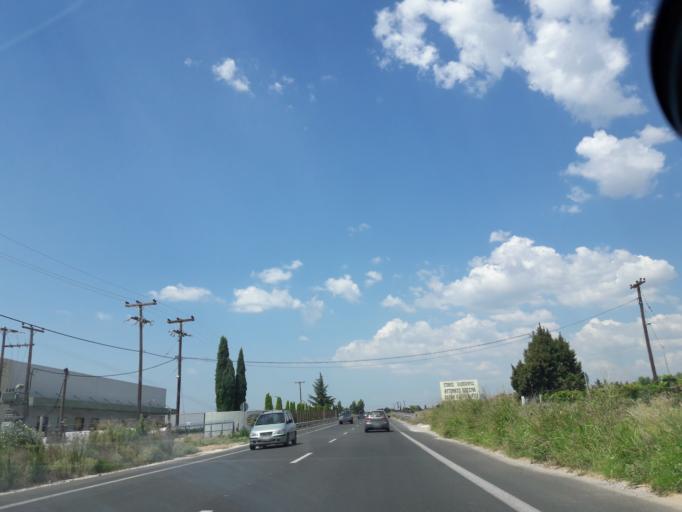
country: GR
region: Central Macedonia
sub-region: Nomos Thessalonikis
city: Agia Paraskevi
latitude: 40.5185
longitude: 23.0634
